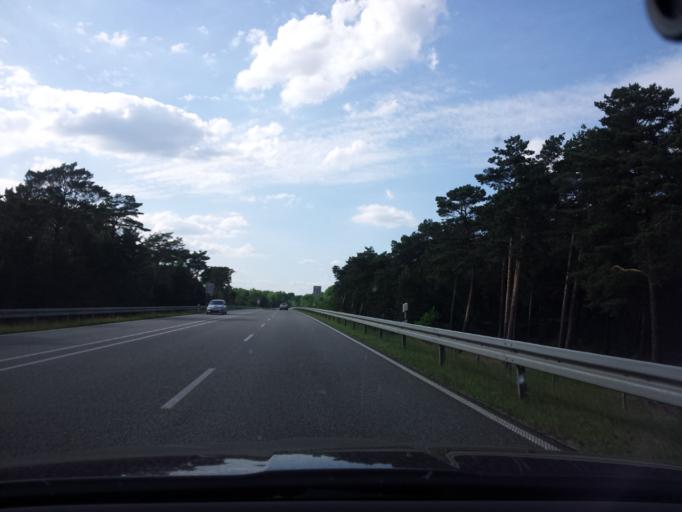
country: DE
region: Brandenburg
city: Luckenwalde
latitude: 52.0839
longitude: 13.1279
